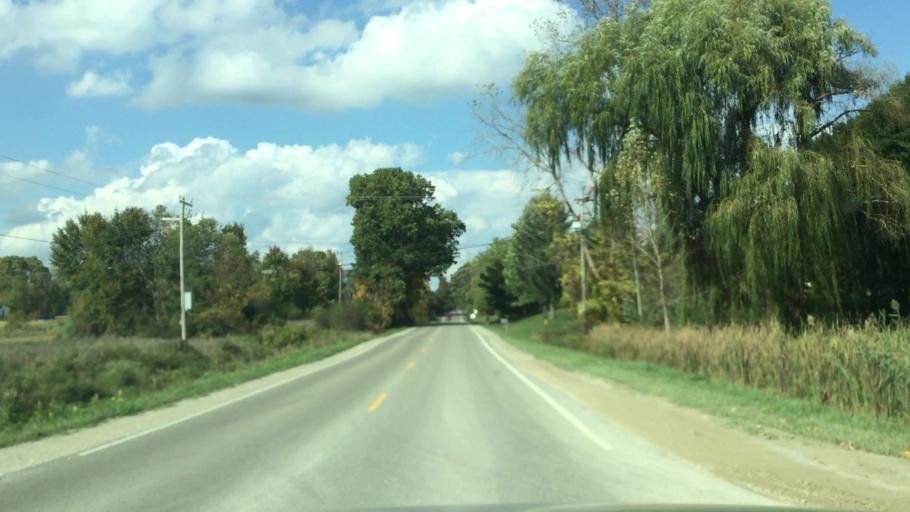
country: US
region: Michigan
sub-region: Genesee County
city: Fenton
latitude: 42.6788
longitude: -83.7022
